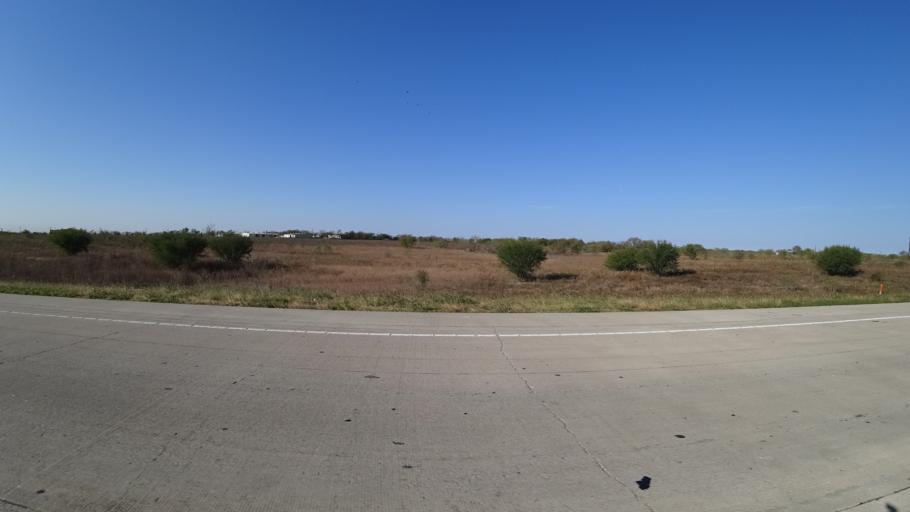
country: US
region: Texas
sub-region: Travis County
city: Manor
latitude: 30.3943
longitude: -97.5797
